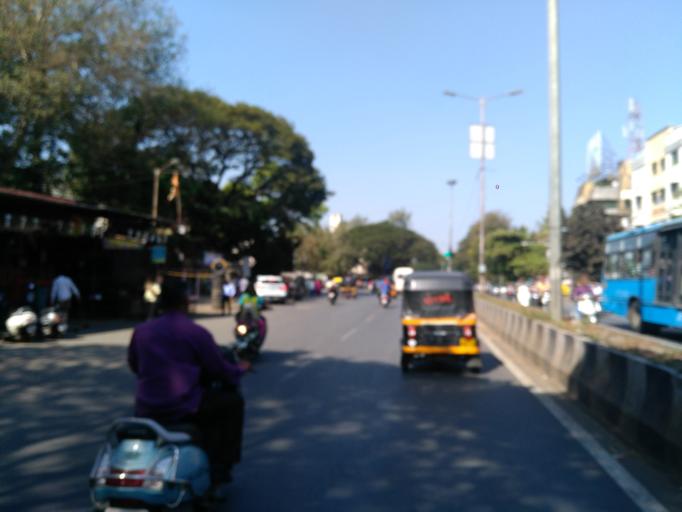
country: IN
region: Maharashtra
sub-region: Pune Division
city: Pune
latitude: 18.4683
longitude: 73.8642
